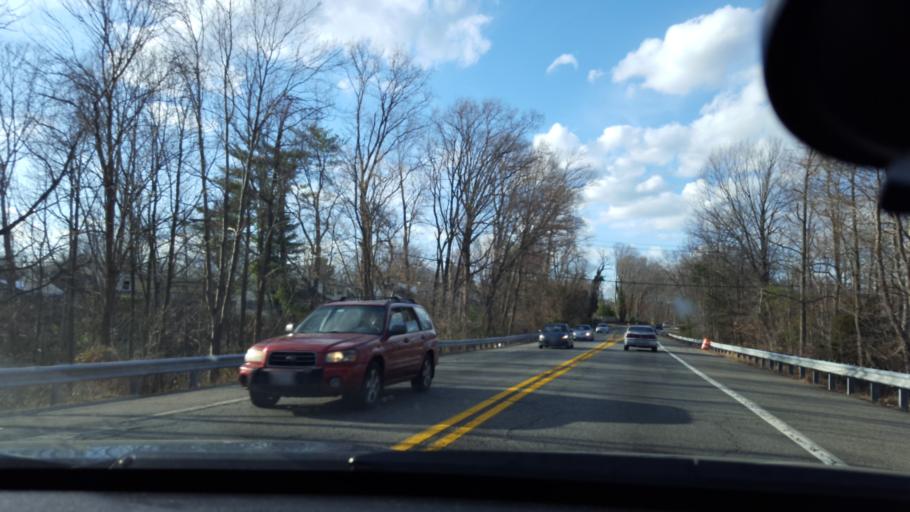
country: US
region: Maryland
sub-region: Prince George's County
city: Bowie
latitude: 38.9609
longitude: -76.7500
